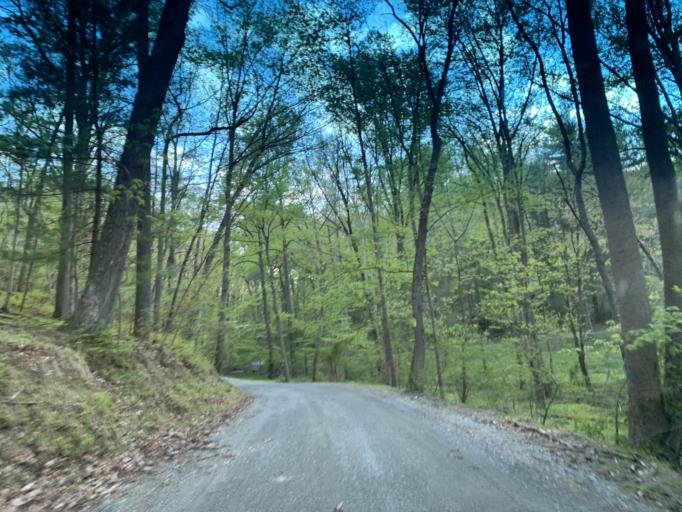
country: US
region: Maryland
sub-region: Harford County
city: Jarrettsville
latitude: 39.6285
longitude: -76.4278
